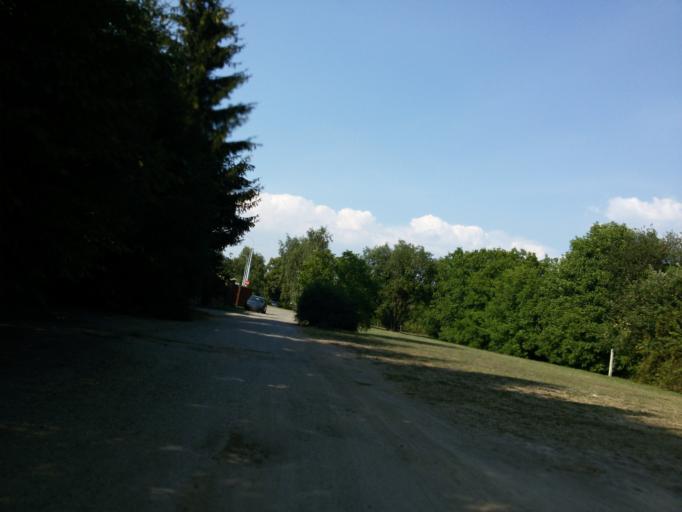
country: CZ
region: South Moravian
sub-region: Mesto Brno
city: Mokra Hora
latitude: 49.2520
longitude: 16.5901
